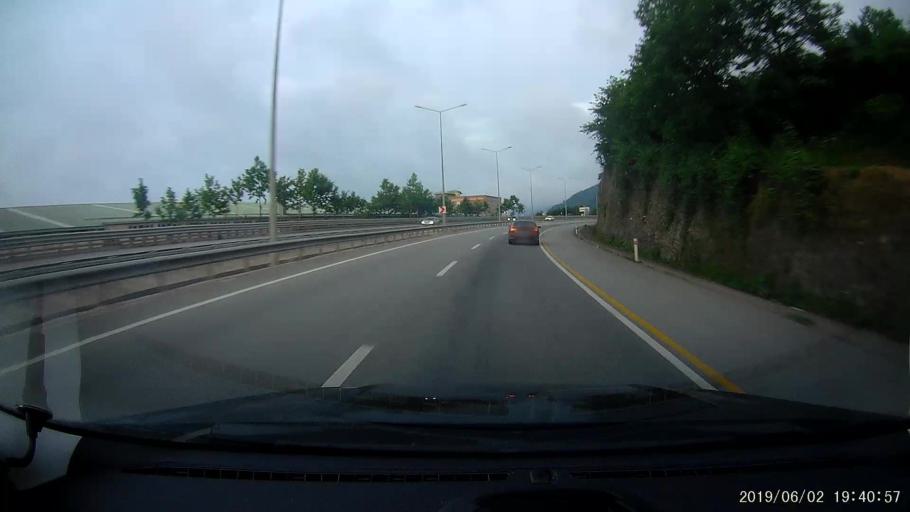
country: TR
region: Giresun
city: Kesap
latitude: 40.9179
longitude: 38.4706
